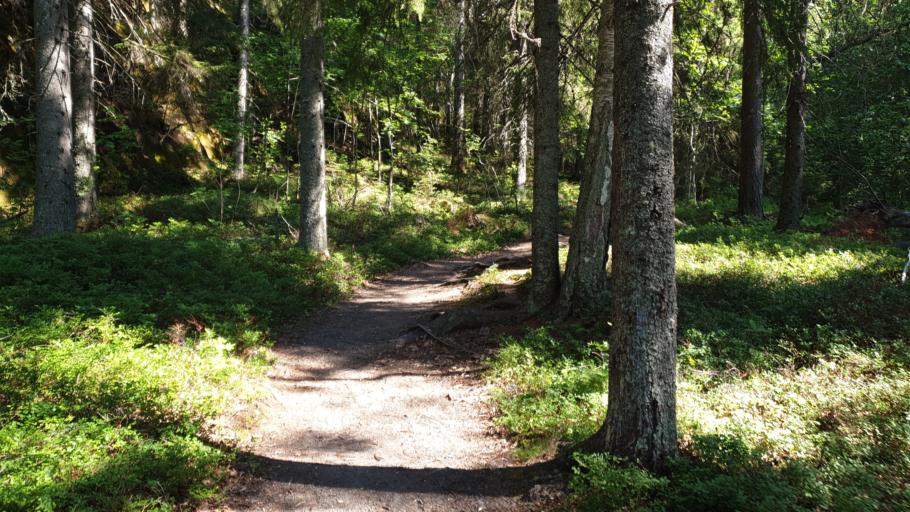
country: SE
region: Vaesternorrland
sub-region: OErnskoeldsviks Kommun
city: Husum
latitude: 63.4974
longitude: 18.9261
